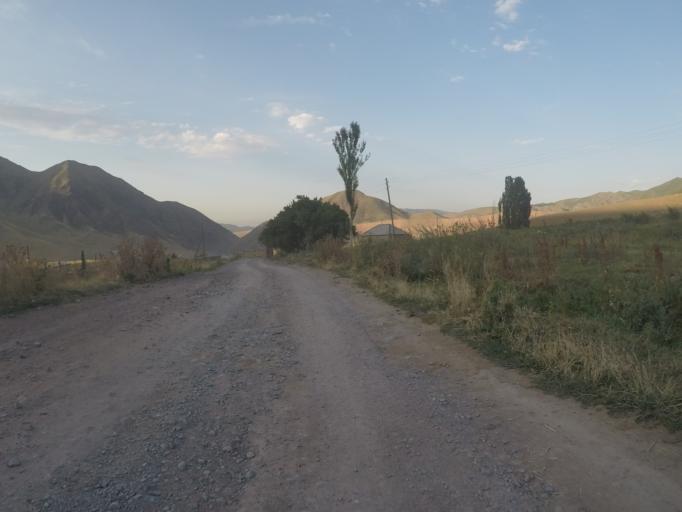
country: KG
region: Chuy
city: Bishkek
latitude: 42.6632
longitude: 74.6495
